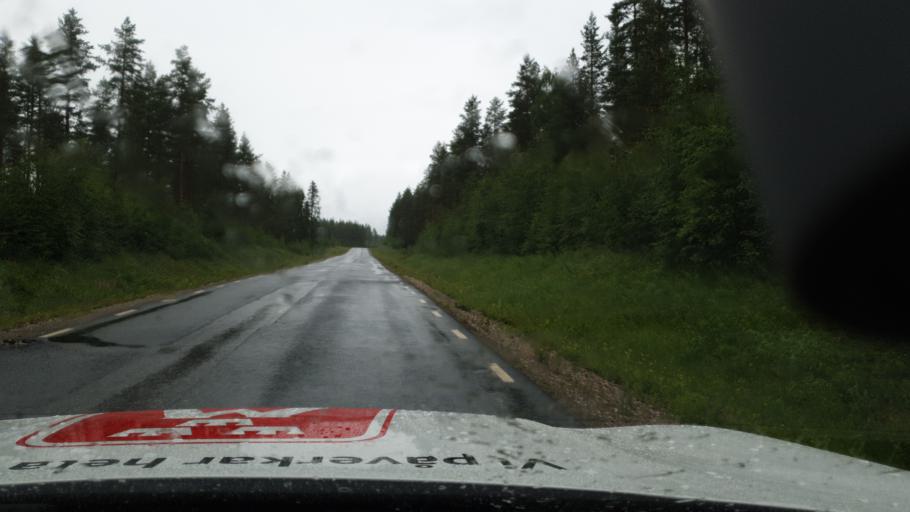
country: SE
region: Vaesterbotten
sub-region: Vindelns Kommun
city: Vindeln
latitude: 64.5502
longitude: 19.9161
